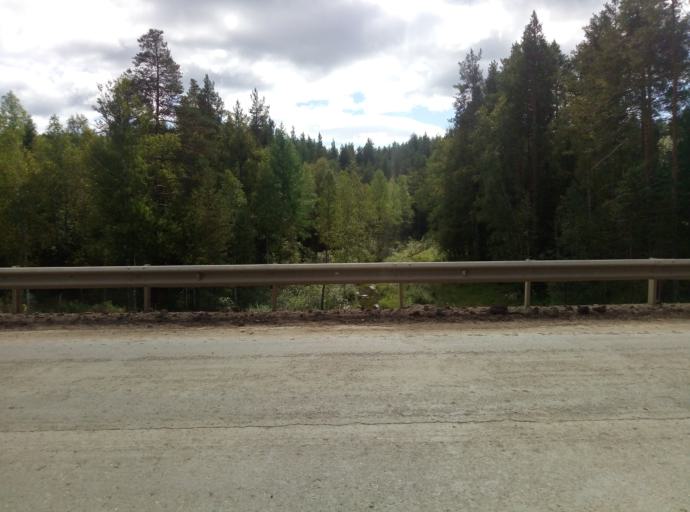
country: RU
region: Sverdlovsk
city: Karpinsk
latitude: 59.6968
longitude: 59.8755
